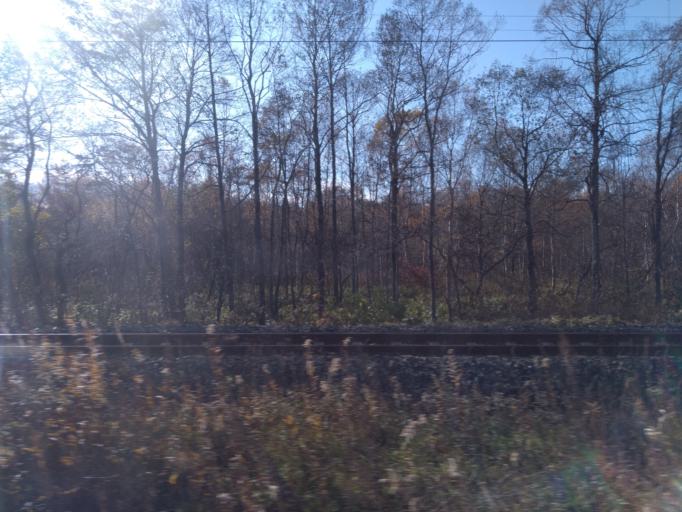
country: JP
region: Hokkaido
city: Chitose
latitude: 42.7636
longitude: 141.7222
